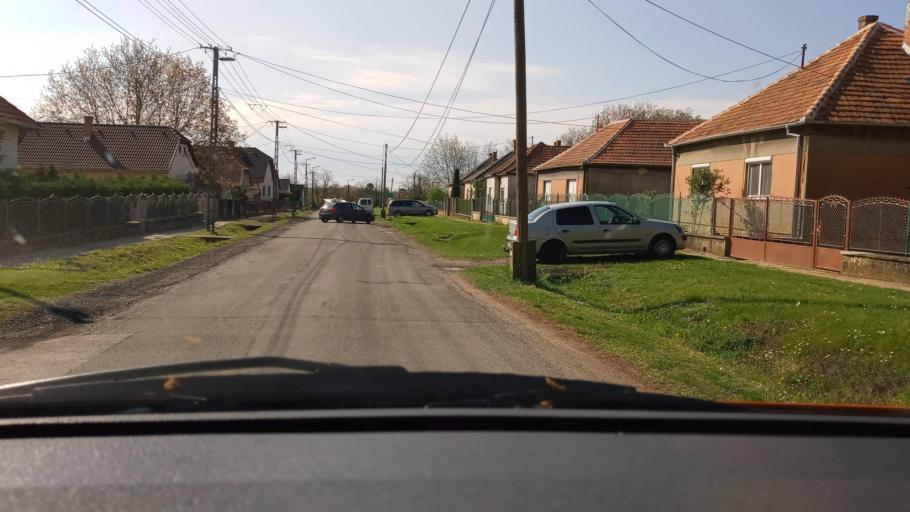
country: HU
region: Baranya
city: Hosszuheteny
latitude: 46.1136
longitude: 18.3413
